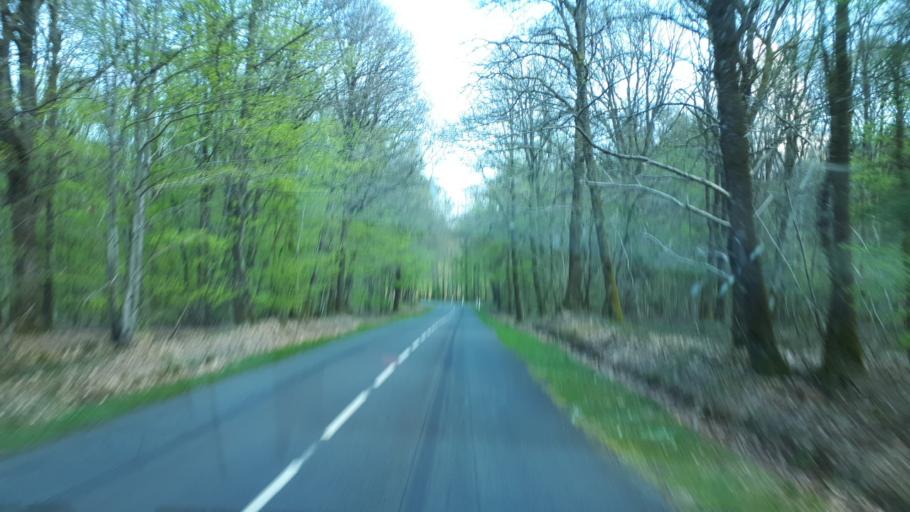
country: FR
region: Centre
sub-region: Departement du Cher
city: Henrichemont
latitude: 47.2983
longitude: 2.6155
